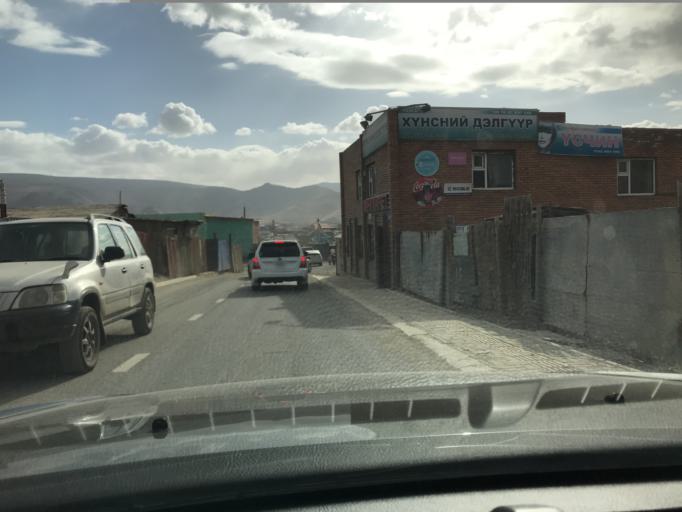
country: MN
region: Ulaanbaatar
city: Ulaanbaatar
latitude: 47.9149
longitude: 106.9640
